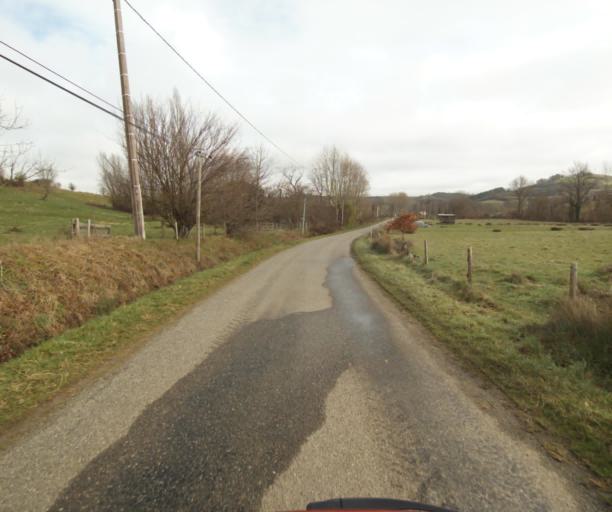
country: FR
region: Midi-Pyrenees
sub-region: Departement de la Haute-Garonne
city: Gaillac-Toulza
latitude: 43.1655
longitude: 1.4884
